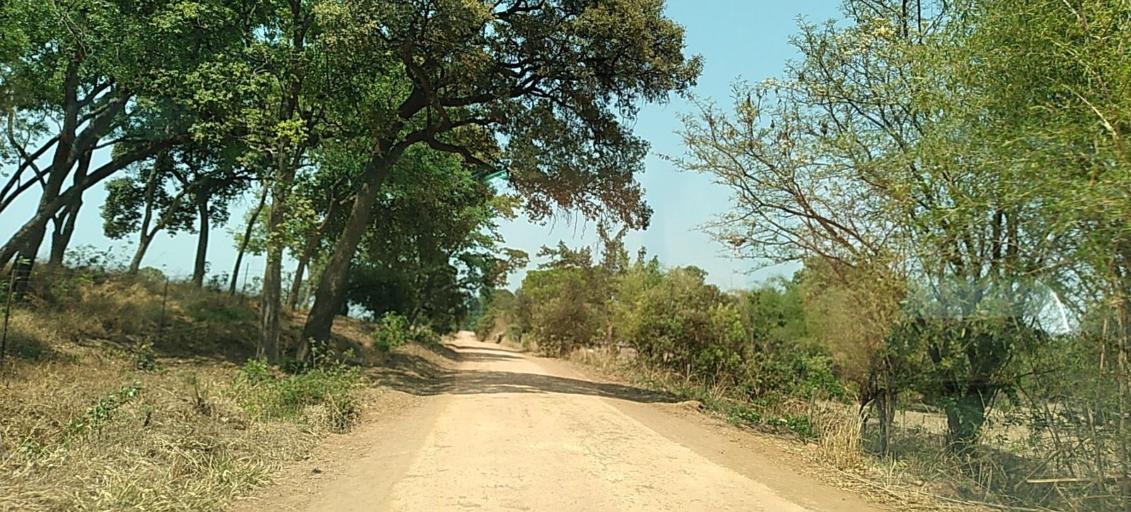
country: ZM
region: Copperbelt
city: Chambishi
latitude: -12.6233
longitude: 27.9524
